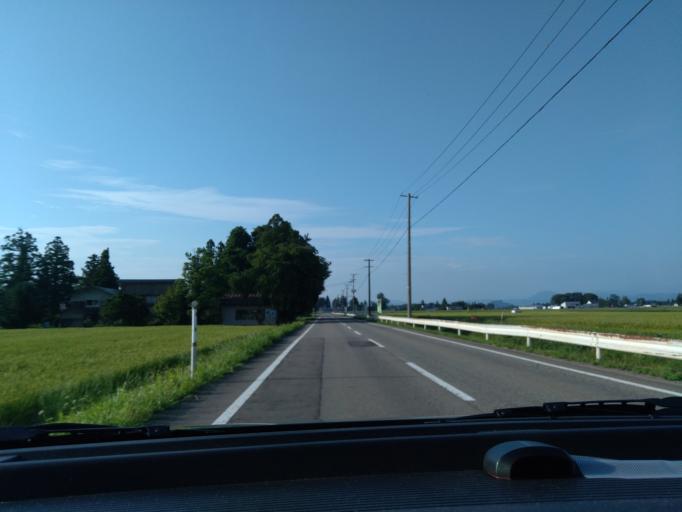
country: JP
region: Akita
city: Kakunodatemachi
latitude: 39.5224
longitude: 140.5581
